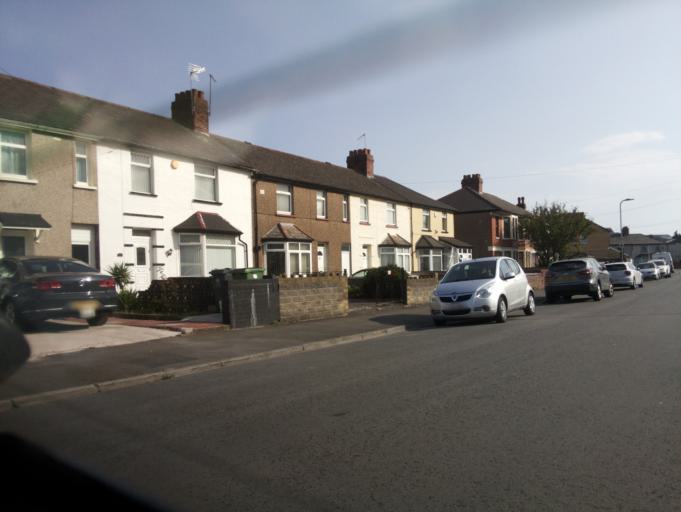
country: GB
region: Wales
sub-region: Cardiff
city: Cardiff
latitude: 51.4881
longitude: -3.1425
